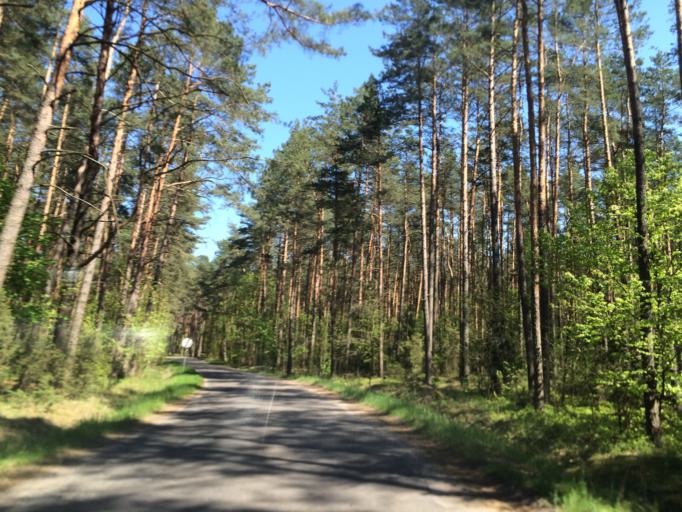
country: PL
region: Kujawsko-Pomorskie
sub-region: Powiat brodnicki
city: Brodnica
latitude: 53.3836
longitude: 19.4247
